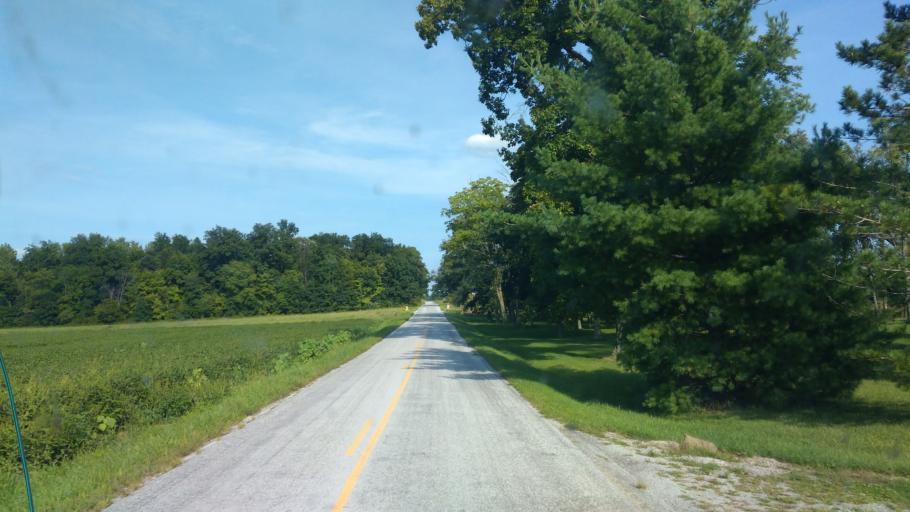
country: US
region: Ohio
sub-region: Hardin County
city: Kenton
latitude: 40.7101
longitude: -83.5877
